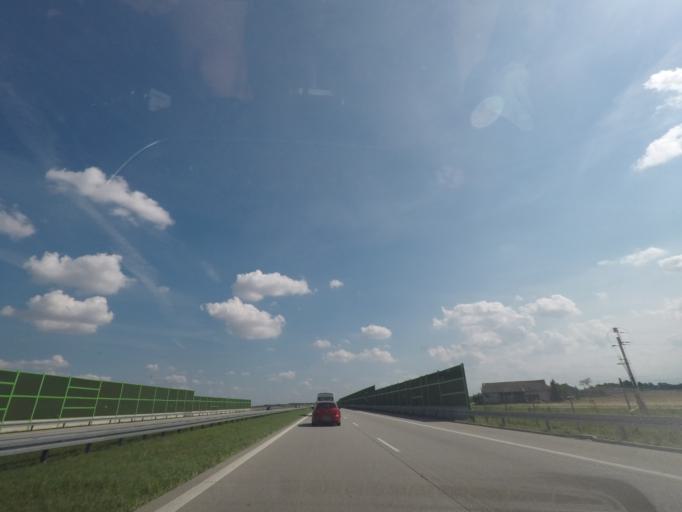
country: PL
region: Lodz Voivodeship
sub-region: Powiat lodzki wschodni
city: Tuszyn
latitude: 51.6010
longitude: 19.5799
